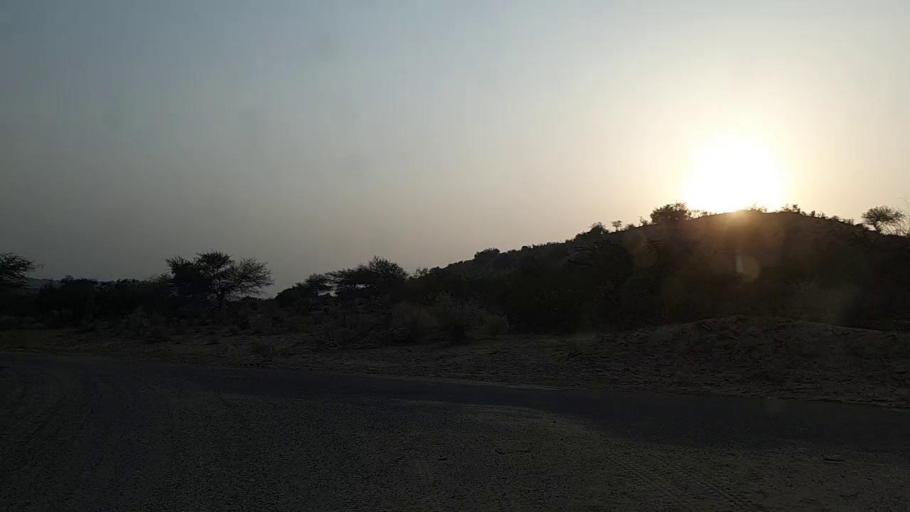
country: PK
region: Sindh
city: Naukot
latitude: 24.6766
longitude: 69.4602
